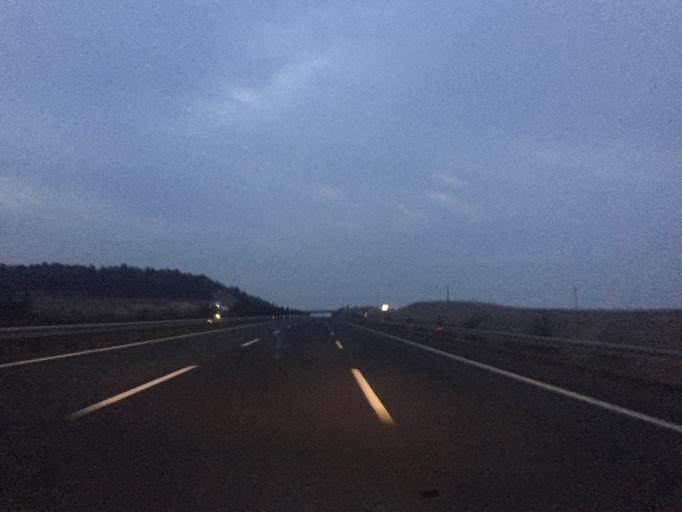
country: TR
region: Sanliurfa
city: Sanliurfa
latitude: 37.1978
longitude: 38.9277
